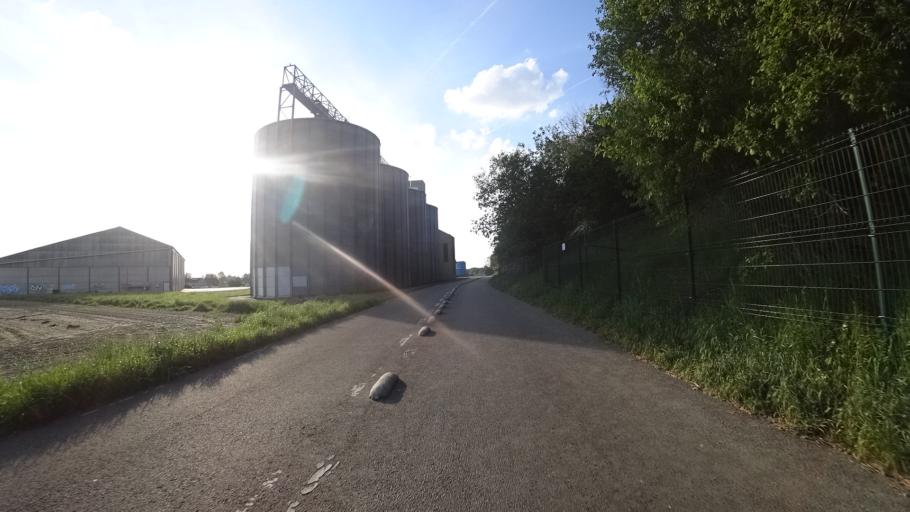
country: BE
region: Wallonia
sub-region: Province de Namur
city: Eghezee
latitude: 50.5694
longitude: 4.9055
